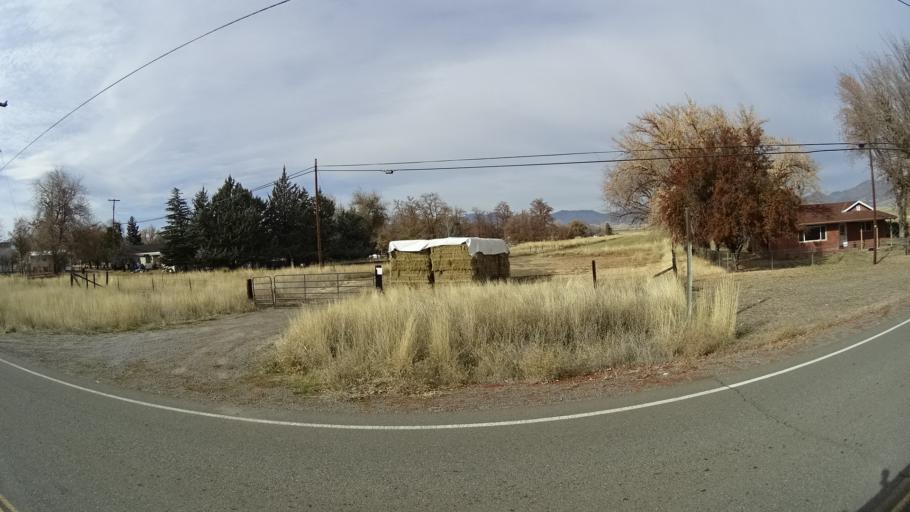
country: US
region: California
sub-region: Siskiyou County
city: Montague
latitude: 41.7315
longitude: -122.5256
